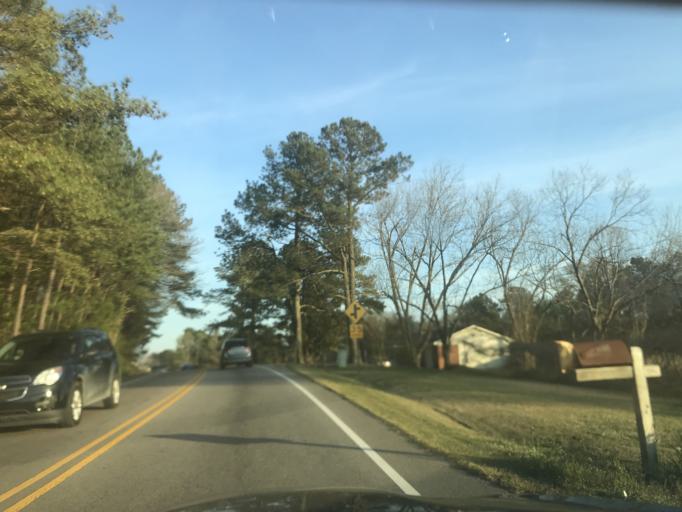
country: US
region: North Carolina
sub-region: Wake County
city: Garner
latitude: 35.7317
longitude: -78.5588
